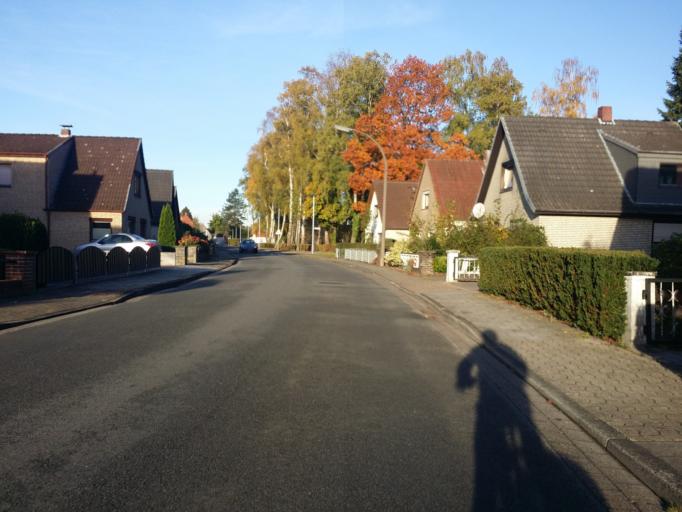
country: DE
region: Lower Saxony
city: Delmenhorst
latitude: 53.0283
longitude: 8.6428
